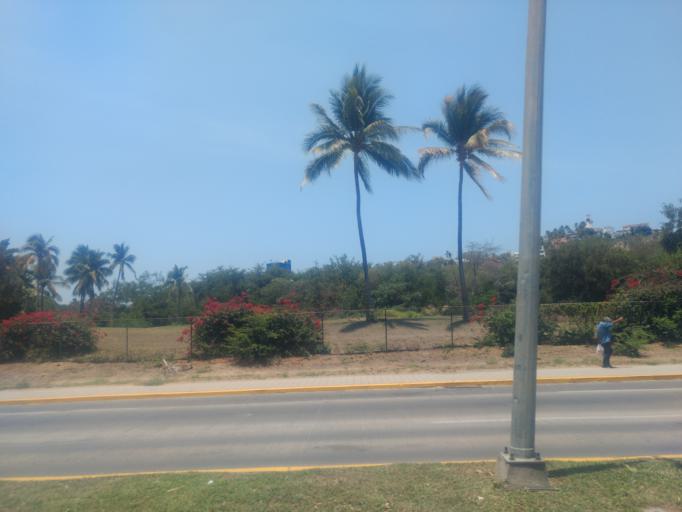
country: MX
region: Colima
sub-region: Manzanillo
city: Manzanillo
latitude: 19.1140
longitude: -104.3440
